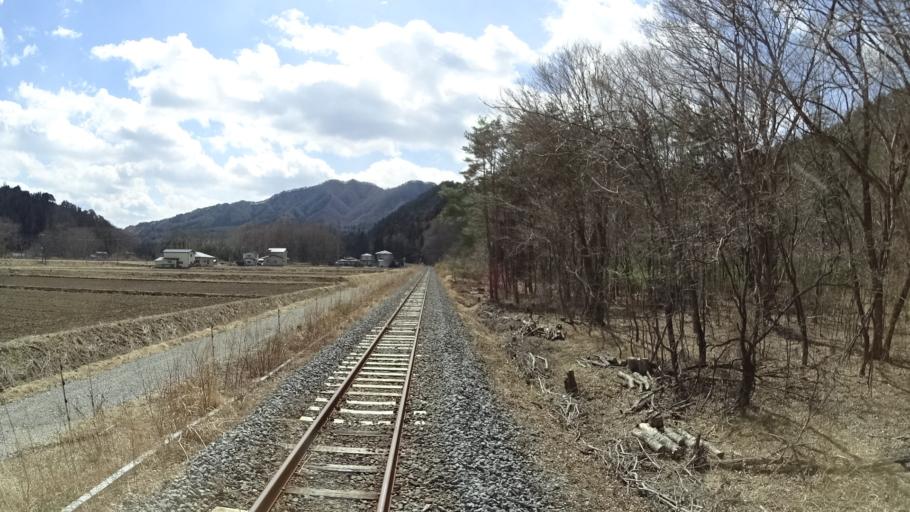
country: JP
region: Iwate
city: Yamada
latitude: 39.5204
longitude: 141.9168
